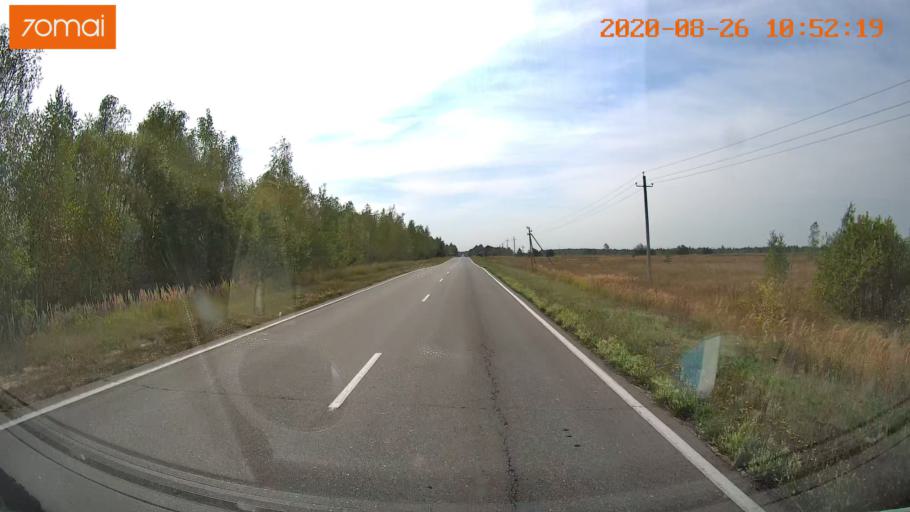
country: RU
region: Rjazan
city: Lashma
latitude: 54.6586
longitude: 41.1536
